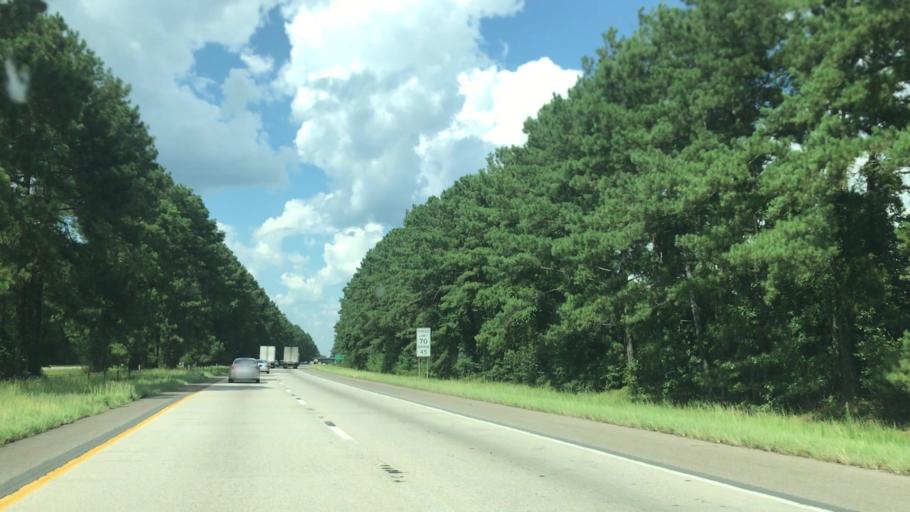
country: US
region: South Carolina
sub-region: Colleton County
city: Walterboro
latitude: 32.8896
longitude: -80.7128
